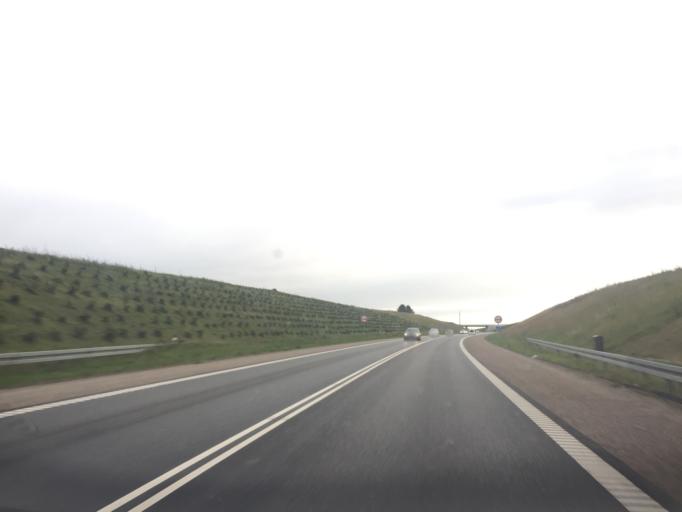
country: DK
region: Capital Region
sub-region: Egedal Kommune
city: Smorumnedre
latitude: 55.7368
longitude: 12.2839
